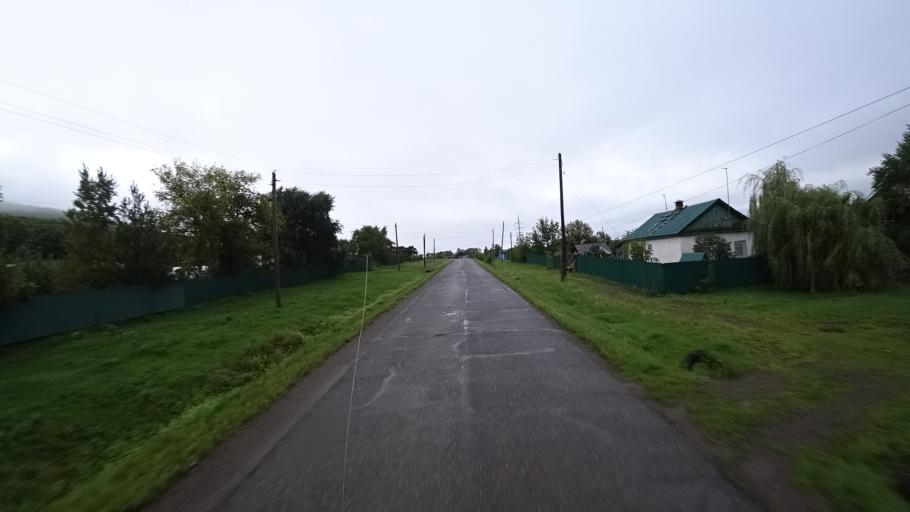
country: RU
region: Primorskiy
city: Monastyrishche
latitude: 44.2608
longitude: 132.4195
